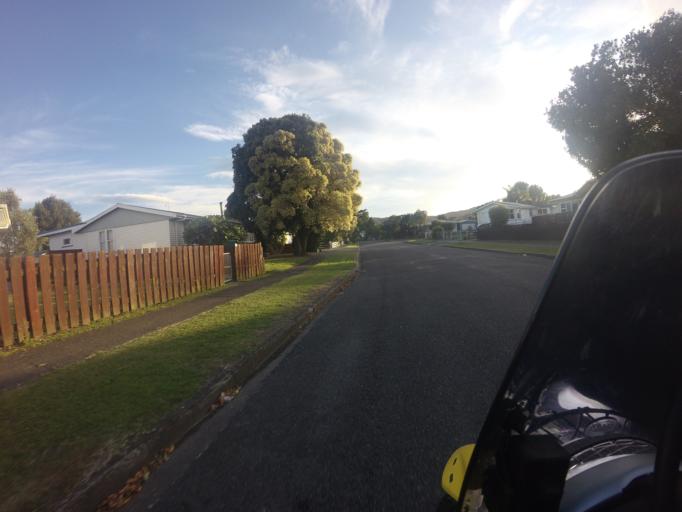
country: NZ
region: Gisborne
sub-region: Gisborne District
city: Gisborne
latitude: -38.6741
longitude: 178.0471
